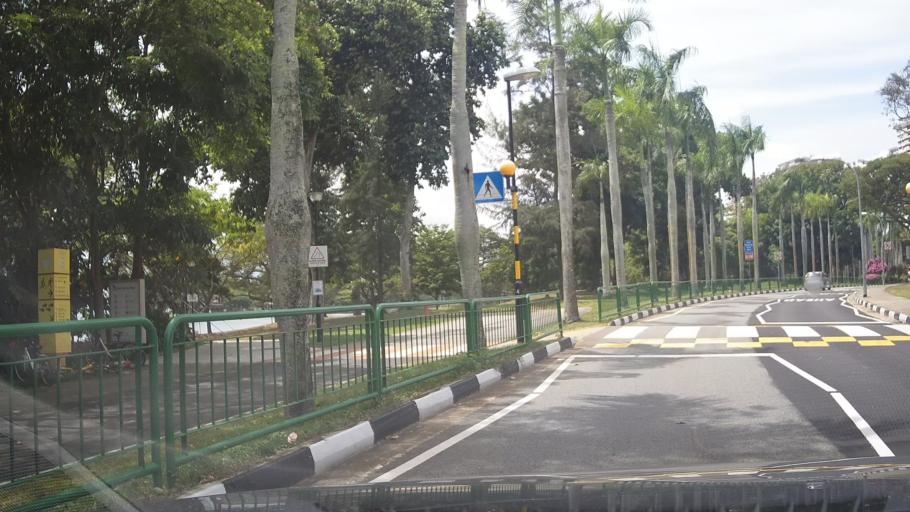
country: SG
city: Singapore
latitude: 1.3075
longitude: 103.9349
